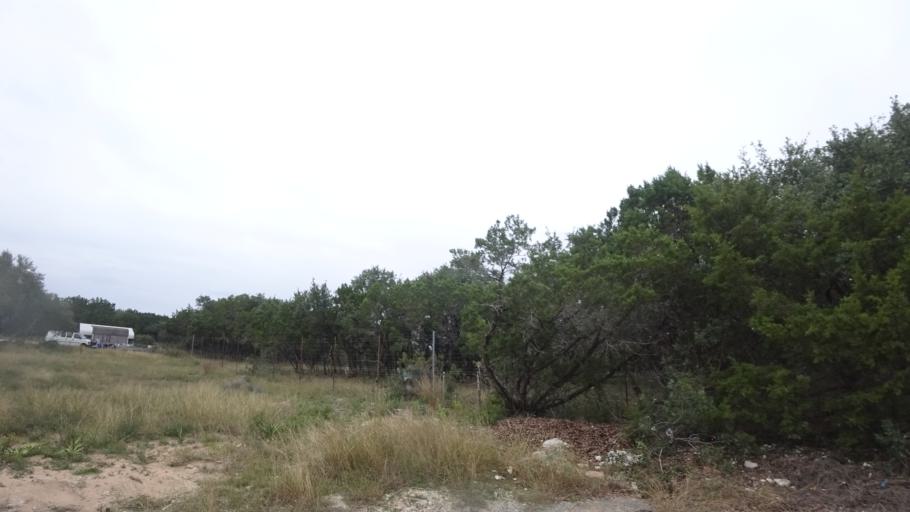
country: US
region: Texas
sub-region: Travis County
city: Lakeway
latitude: 30.3705
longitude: -97.9389
